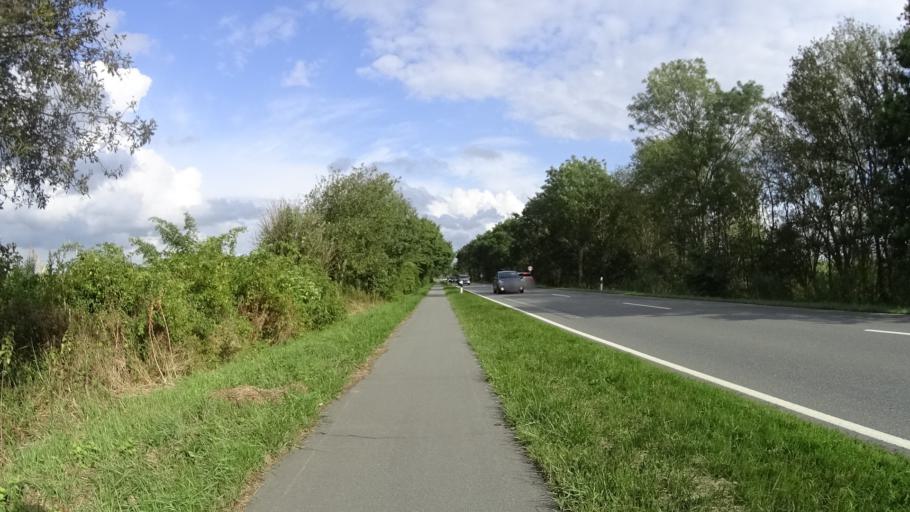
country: DE
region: Lower Saxony
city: Varel
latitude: 53.3888
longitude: 8.1971
